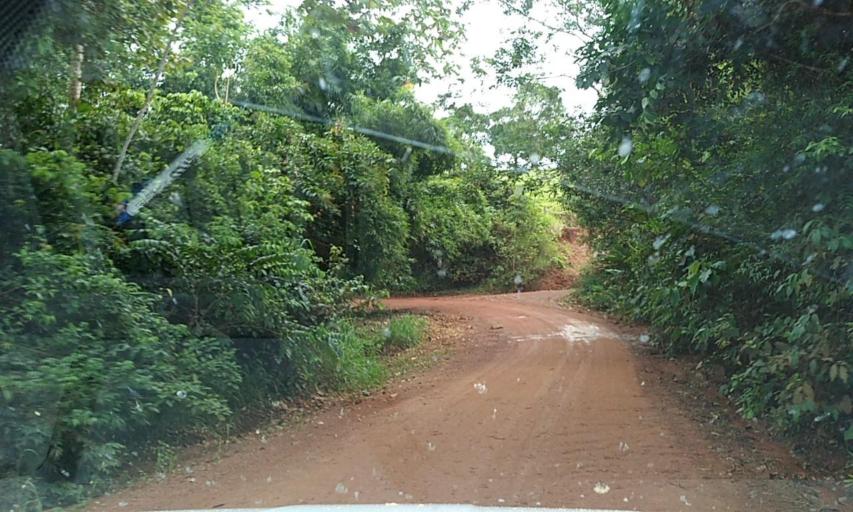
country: BR
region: Para
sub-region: Altamira
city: Altamira
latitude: -3.3092
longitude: -52.6866
